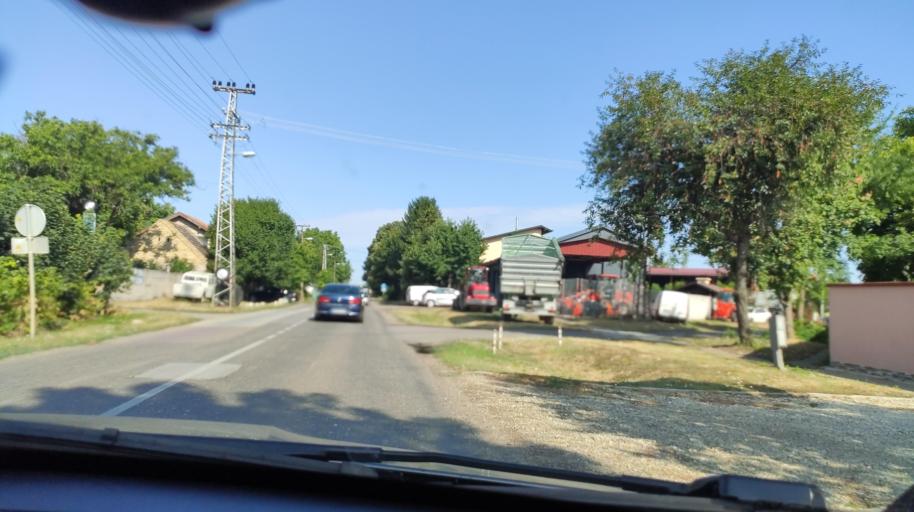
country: RS
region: Autonomna Pokrajina Vojvodina
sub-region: Severnobacki Okrug
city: Backa Topola
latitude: 45.8143
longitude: 19.6189
